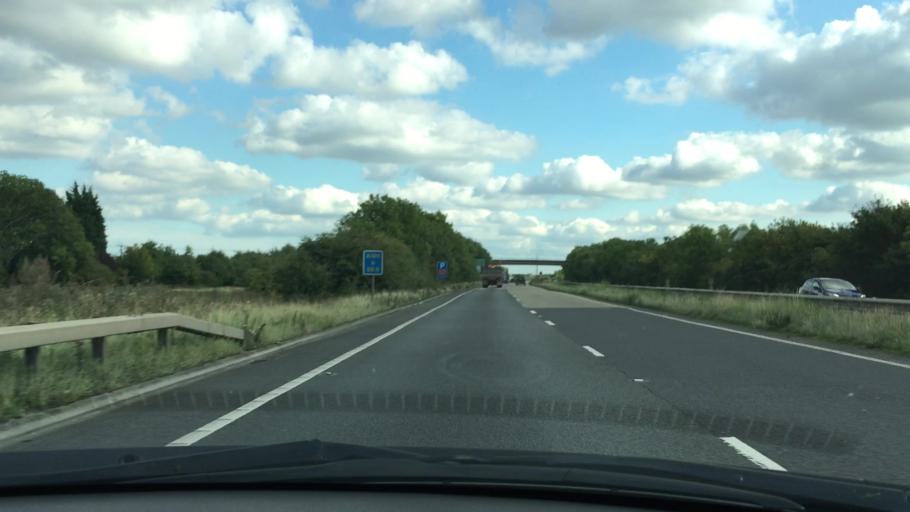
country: GB
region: England
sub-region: North East Lincolnshire
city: Healing
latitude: 53.5901
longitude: -0.1607
